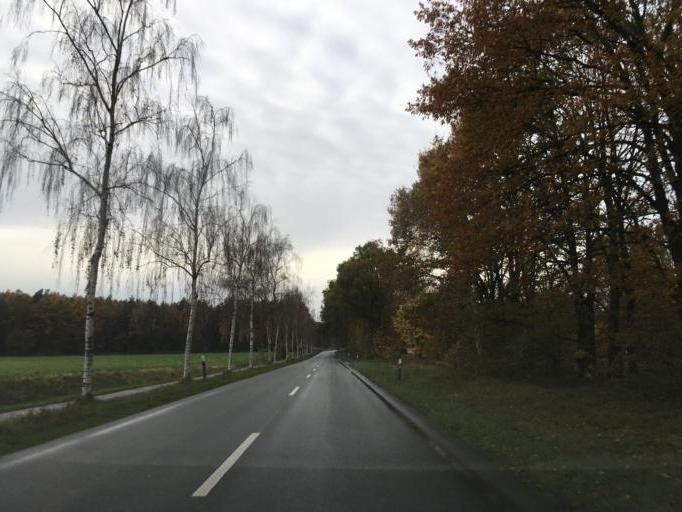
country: DE
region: Lower Saxony
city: Oldendorf
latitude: 53.1773
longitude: 10.2248
